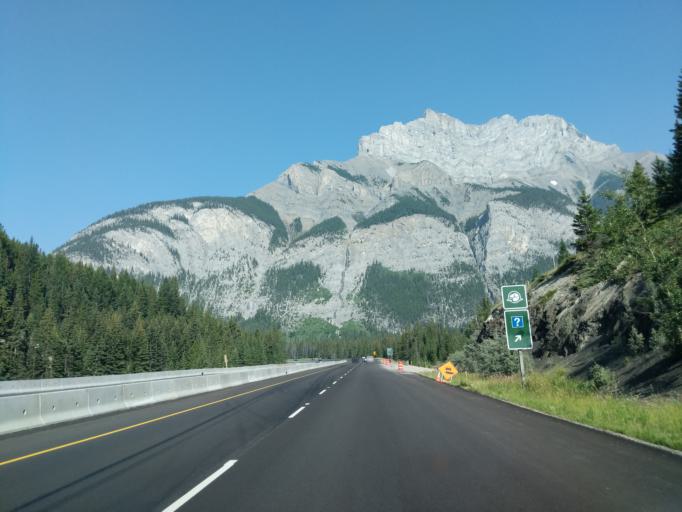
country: CA
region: Alberta
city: Banff
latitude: 51.2073
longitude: -115.5263
